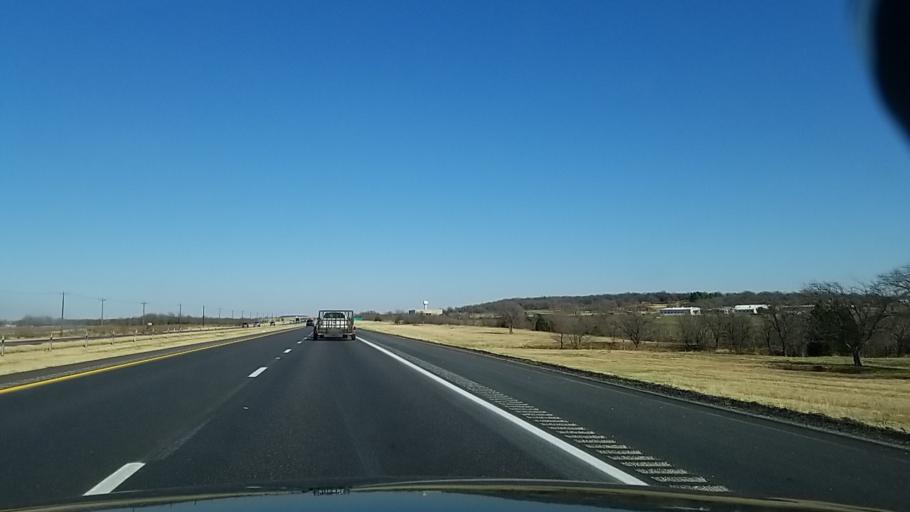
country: US
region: Texas
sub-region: Denton County
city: Argyle
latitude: 33.1086
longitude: -97.2197
